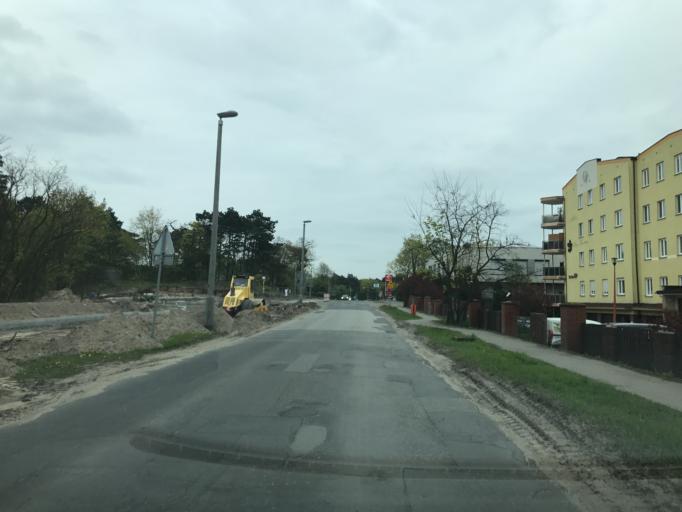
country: PL
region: Kujawsko-Pomorskie
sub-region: Torun
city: Torun
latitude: 53.0347
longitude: 18.5825
